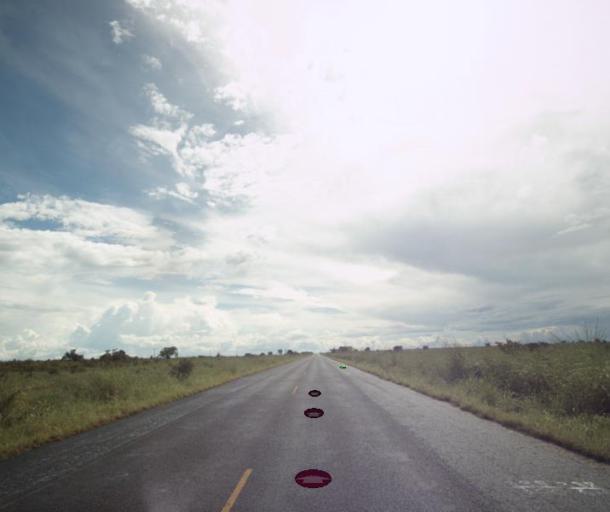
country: BR
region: Goias
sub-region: Sao Miguel Do Araguaia
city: Sao Miguel do Araguaia
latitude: -13.2955
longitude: -50.3620
